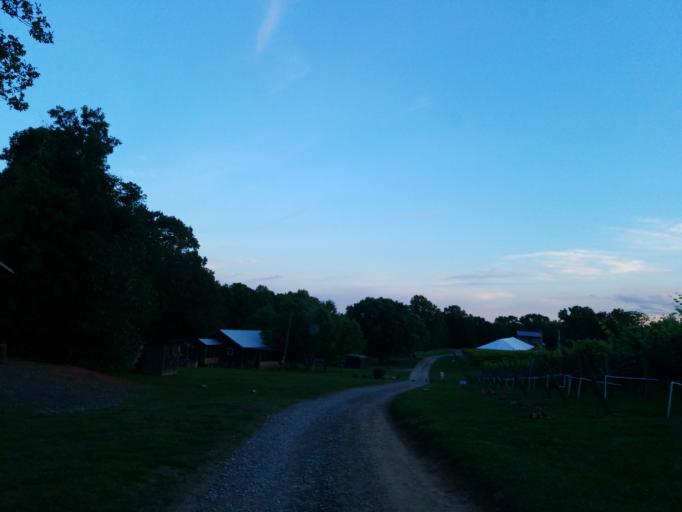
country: US
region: Georgia
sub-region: Lumpkin County
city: Dahlonega
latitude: 34.5585
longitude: -83.9087
